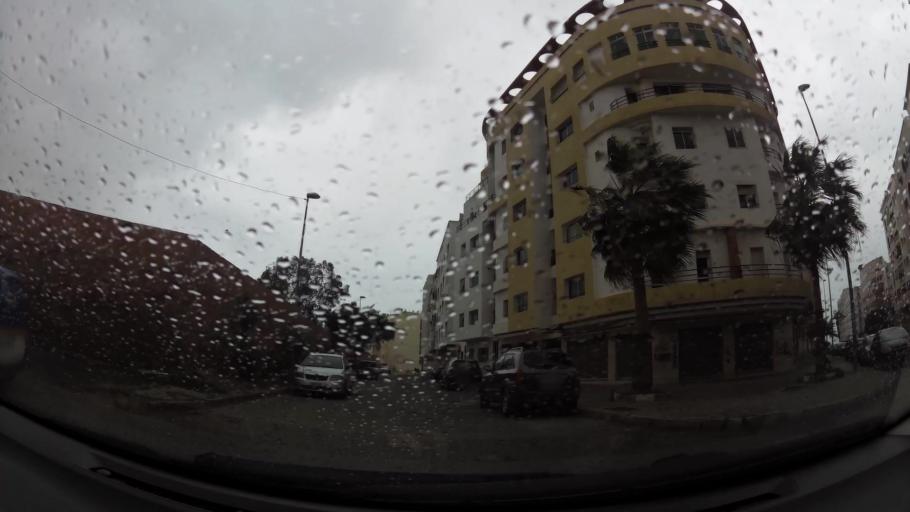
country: MA
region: Grand Casablanca
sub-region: Casablanca
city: Casablanca
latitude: 33.6011
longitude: -7.6457
